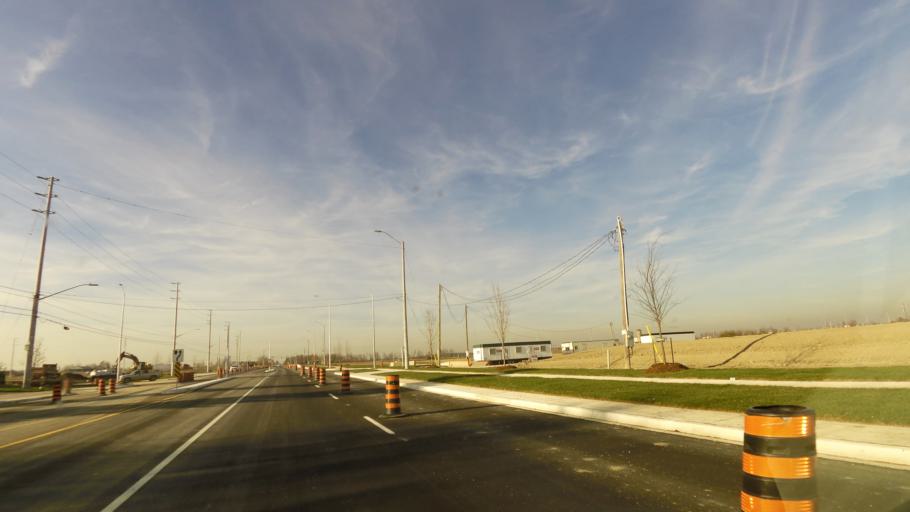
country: CA
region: Ontario
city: Brampton
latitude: 43.7803
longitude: -79.7690
